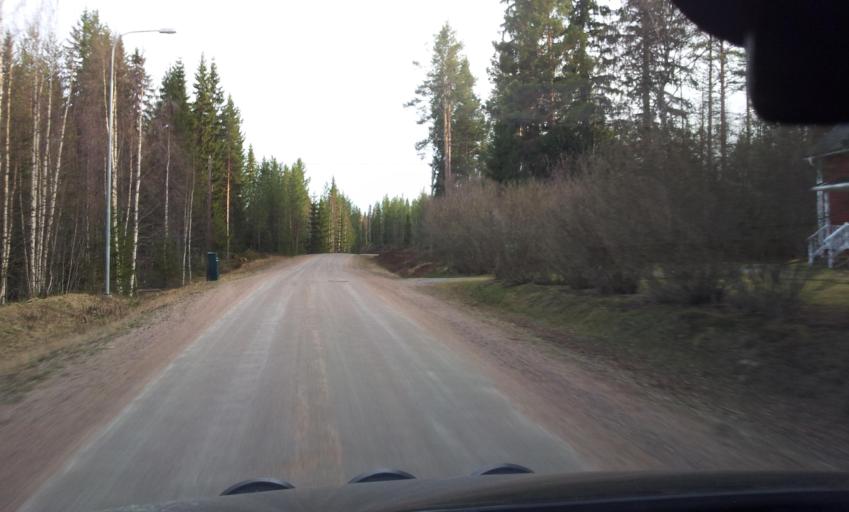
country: SE
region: Vaesternorrland
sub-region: Ange Kommun
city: Ange
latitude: 62.1413
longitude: 15.6609
